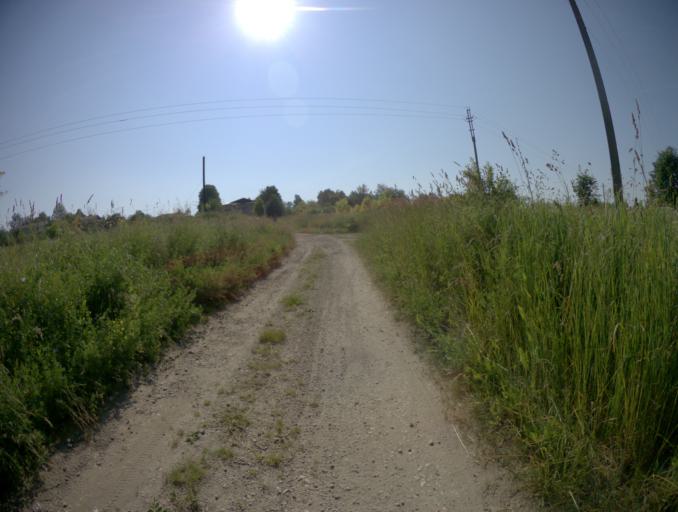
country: RU
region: Vladimir
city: Novovyazniki
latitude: 56.1939
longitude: 42.2470
